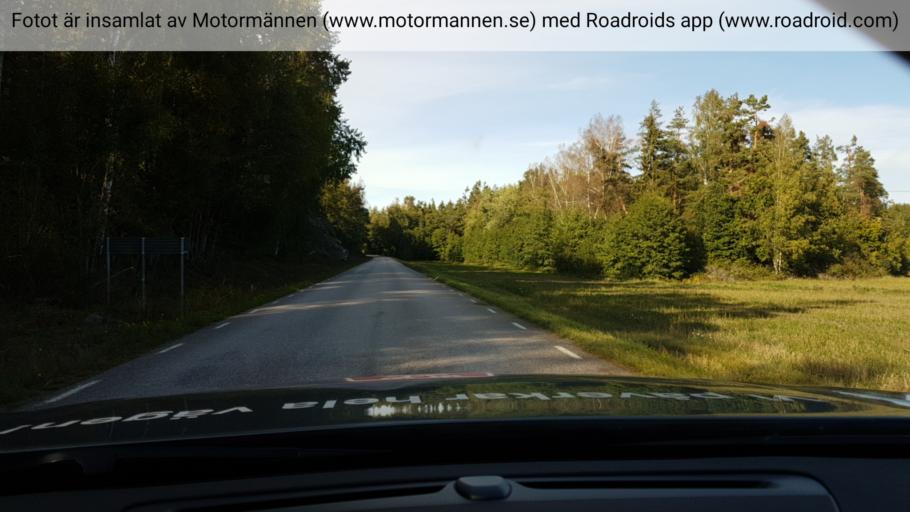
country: SE
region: OEstergoetland
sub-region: Valdemarsviks Kommun
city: Valdemarsvik
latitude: 58.0781
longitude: 16.6439
